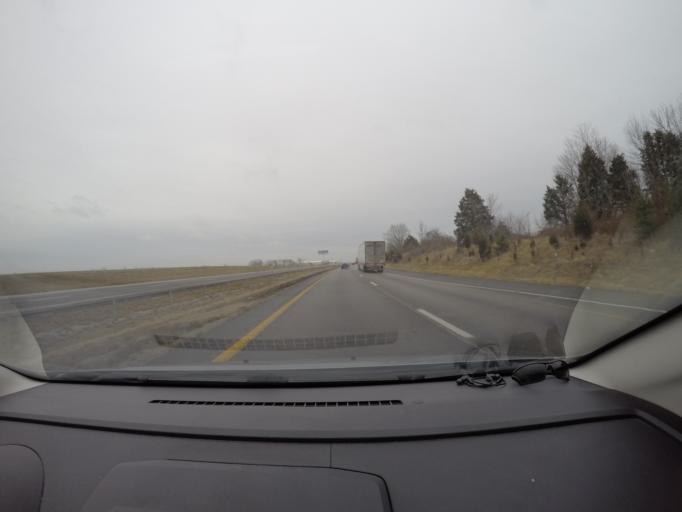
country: US
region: Missouri
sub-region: Warren County
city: Warrenton
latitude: 38.8566
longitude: -91.2989
